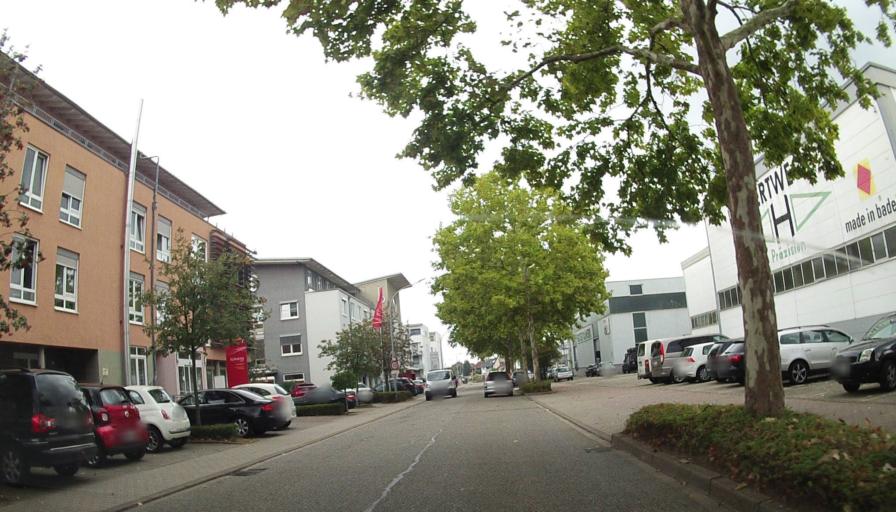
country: DE
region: Baden-Wuerttemberg
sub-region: Karlsruhe Region
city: Gaggenau
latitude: 48.8081
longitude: 8.3200
